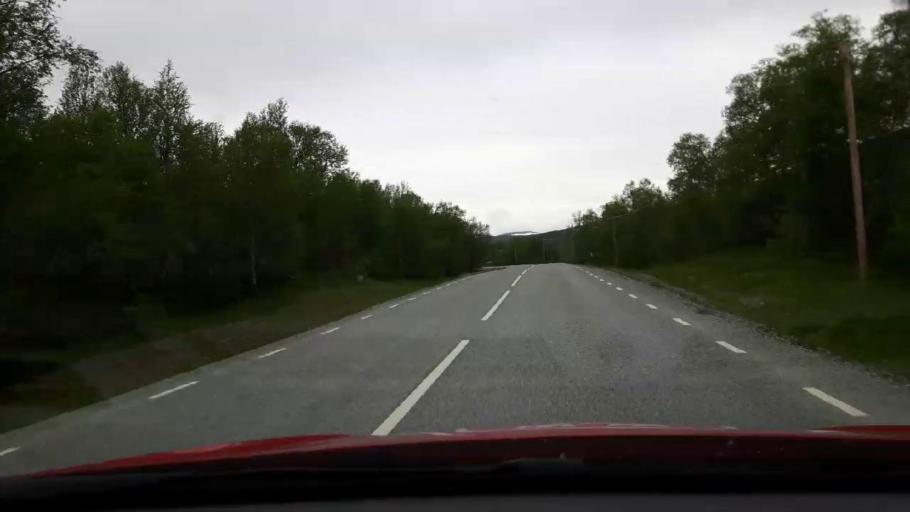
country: NO
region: Sor-Trondelag
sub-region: Tydal
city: Aas
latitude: 62.6921
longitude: 12.4084
